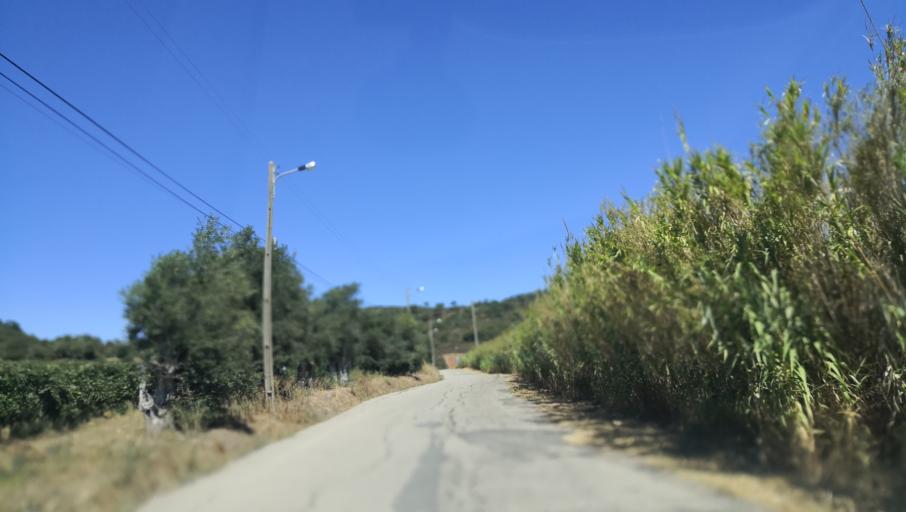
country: PT
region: Setubal
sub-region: Setubal
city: Setubal
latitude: 38.5344
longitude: -8.9140
